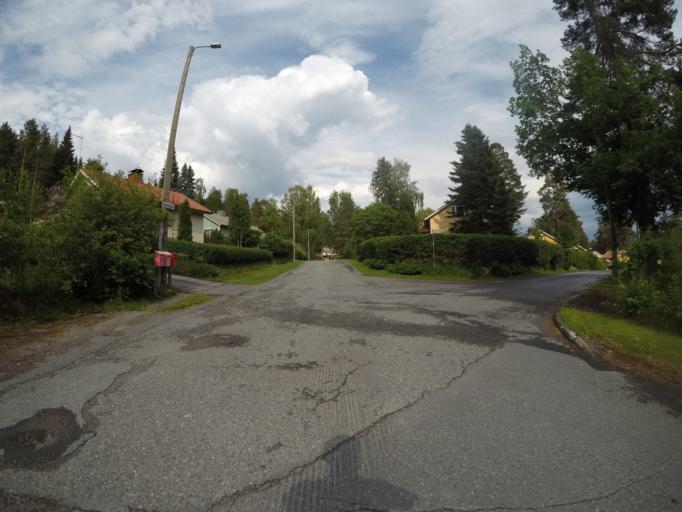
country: FI
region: Haeme
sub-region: Haemeenlinna
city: Haemeenlinna
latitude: 61.0146
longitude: 24.4664
